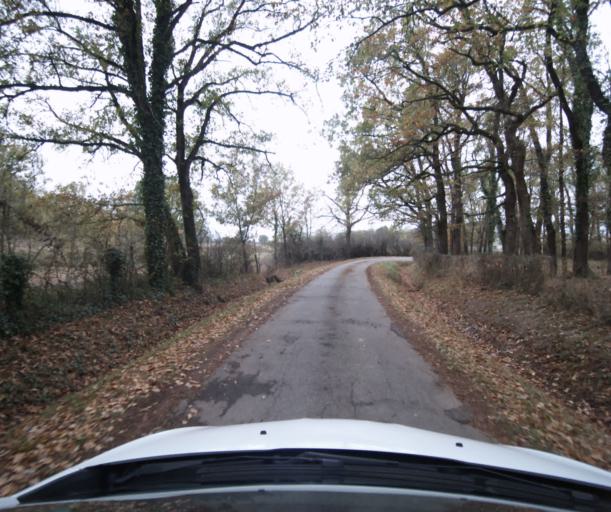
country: FR
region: Midi-Pyrenees
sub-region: Departement du Tarn-et-Garonne
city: Saint-Porquier
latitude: 44.0501
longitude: 1.1628
